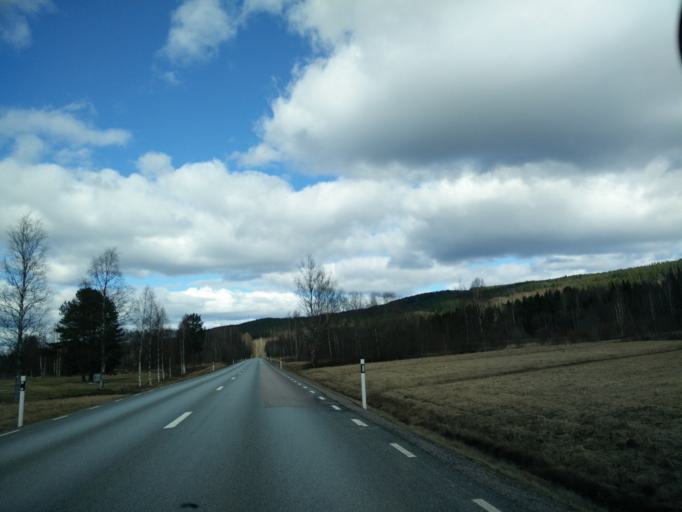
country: SE
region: Vaermland
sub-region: Munkfors Kommun
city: Munkfors
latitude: 59.8784
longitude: 13.5618
